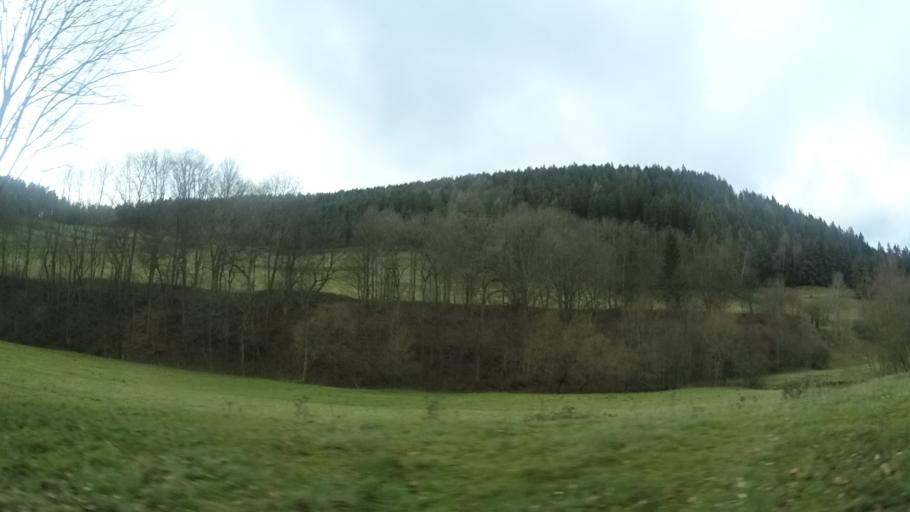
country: DE
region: Thuringia
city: Rohrbach
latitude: 50.6087
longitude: 11.2206
